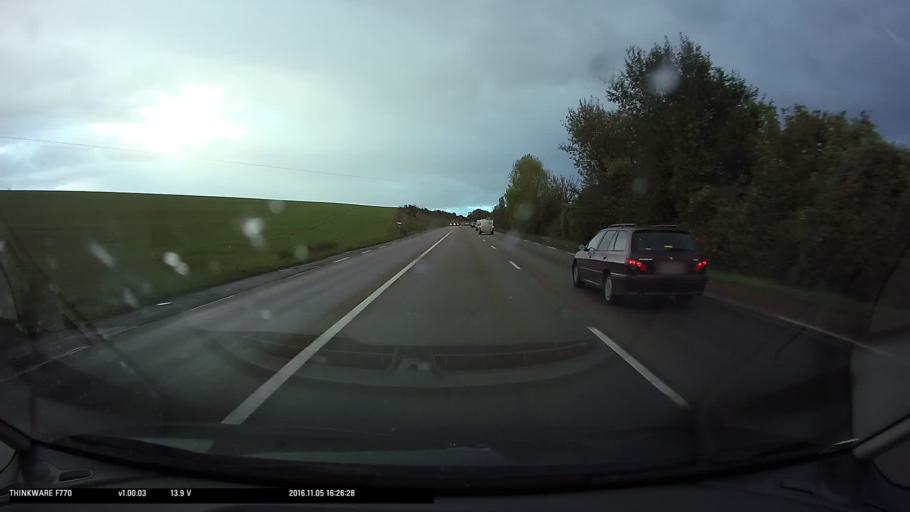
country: FR
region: Ile-de-France
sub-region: Departement des Yvelines
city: Meulan-en-Yvelines
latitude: 49.0198
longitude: 1.9100
